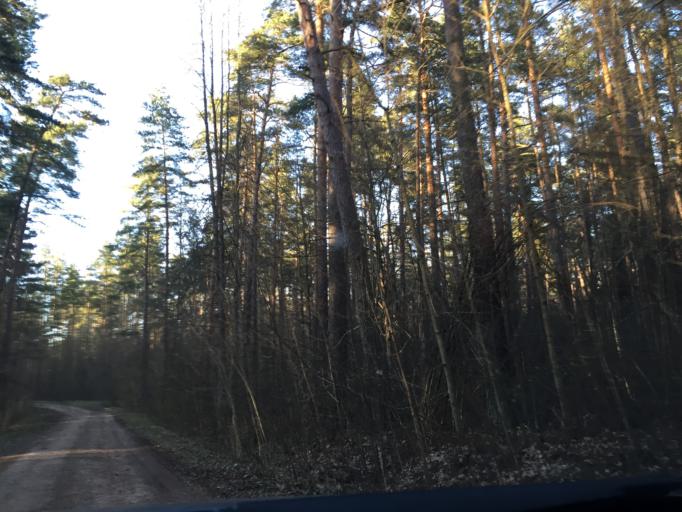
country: LV
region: Kekava
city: Kekava
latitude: 56.8578
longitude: 24.2319
